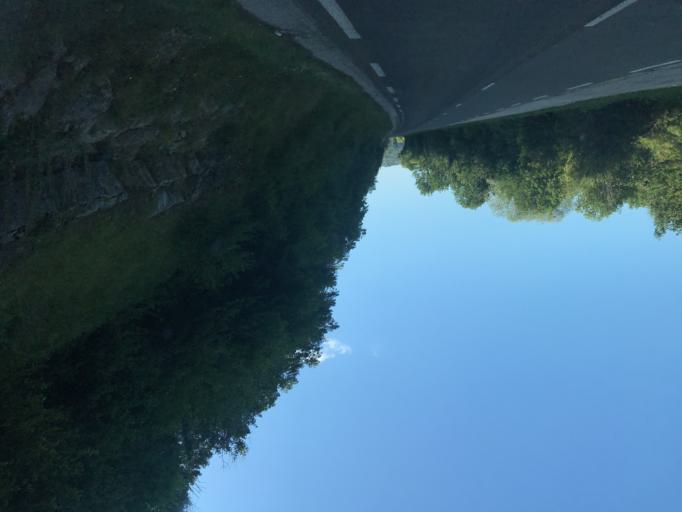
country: FR
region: Franche-Comte
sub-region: Departement du Jura
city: Moirans-en-Montagne
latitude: 46.4016
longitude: 5.7337
